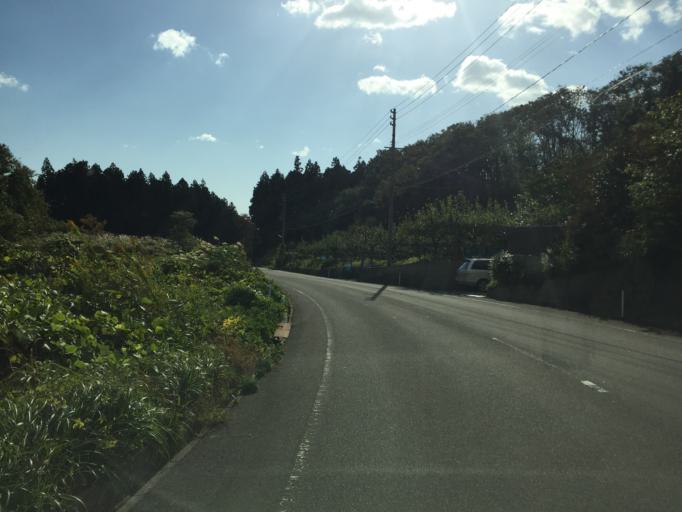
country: JP
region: Fukushima
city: Fukushima-shi
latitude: 37.7969
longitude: 140.3888
